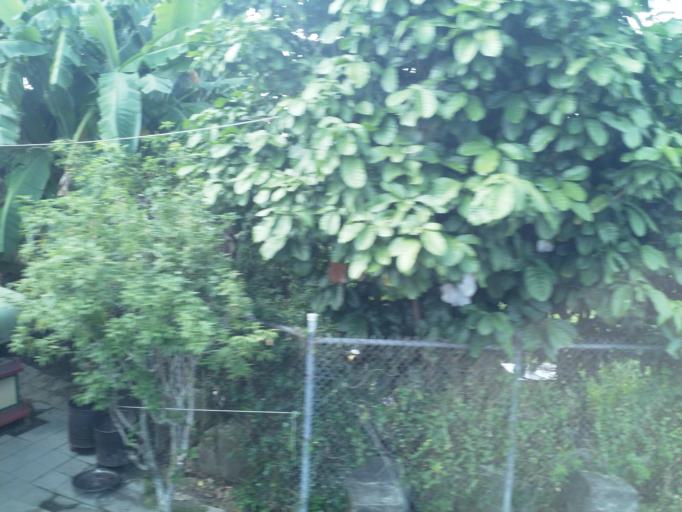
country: TW
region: Taiwan
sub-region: Pingtung
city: Pingtung
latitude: 22.8808
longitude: 120.5756
